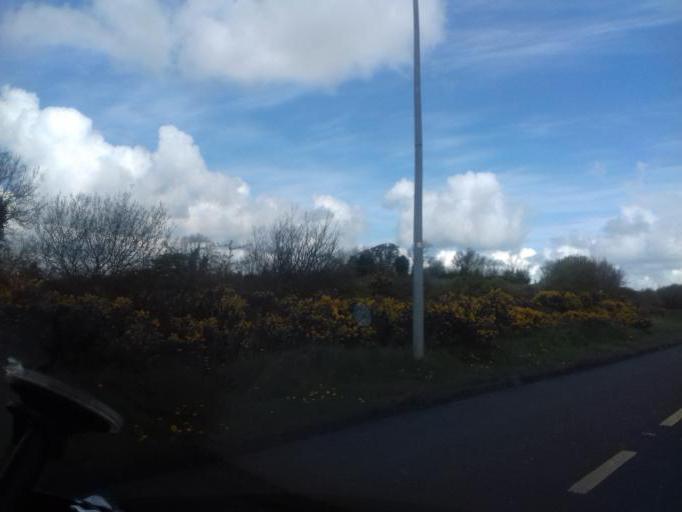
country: IE
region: Ulster
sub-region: An Cabhan
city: Cavan
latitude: 54.0135
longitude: -7.3413
